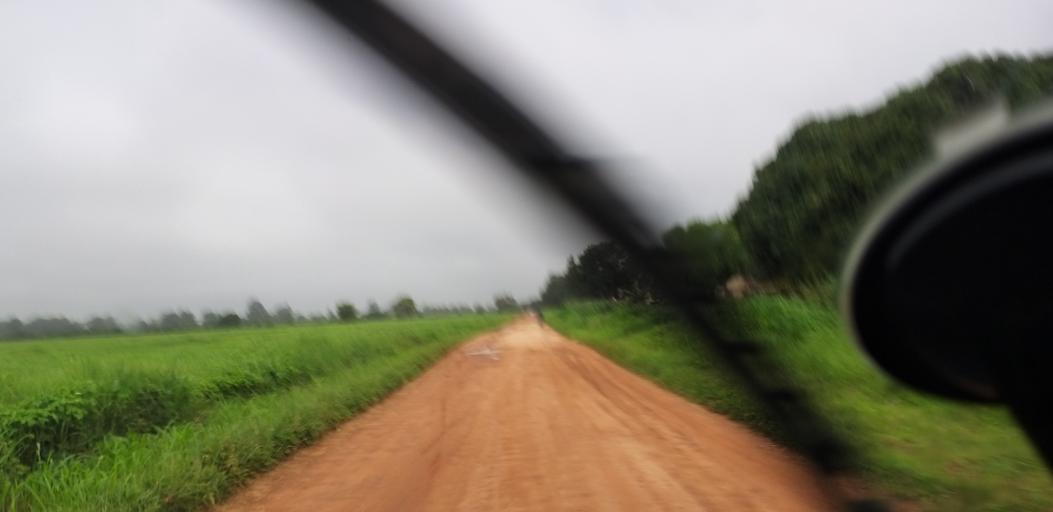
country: ZM
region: Lusaka
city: Lusaka
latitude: -15.5238
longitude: 28.3025
